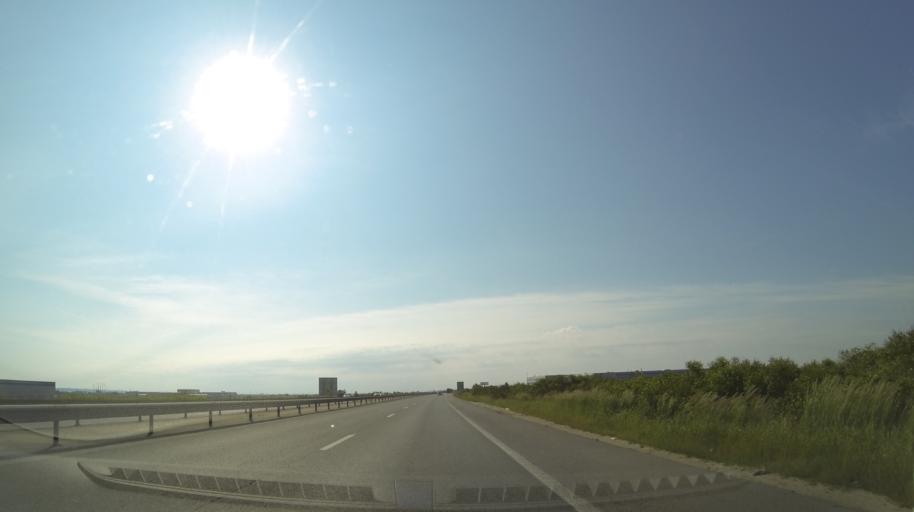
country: RO
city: Oarja Sat
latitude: 44.7956
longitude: 24.9812
